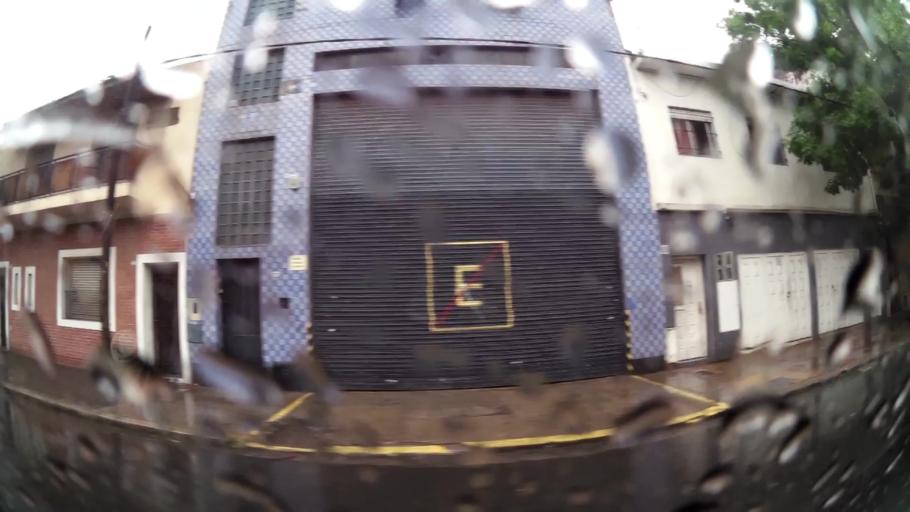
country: AR
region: Buenos Aires
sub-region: Partido de Avellaneda
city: Avellaneda
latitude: -34.6453
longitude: -58.3658
